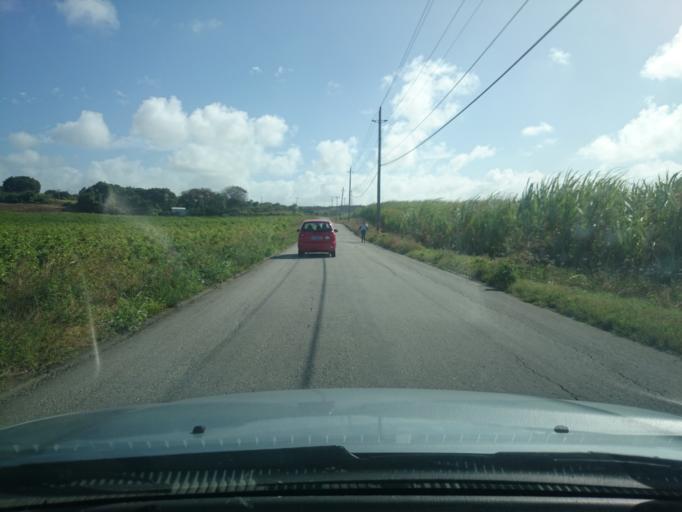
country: BB
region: Saint Lucy
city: Checker Hall
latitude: 13.3039
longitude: -59.6165
